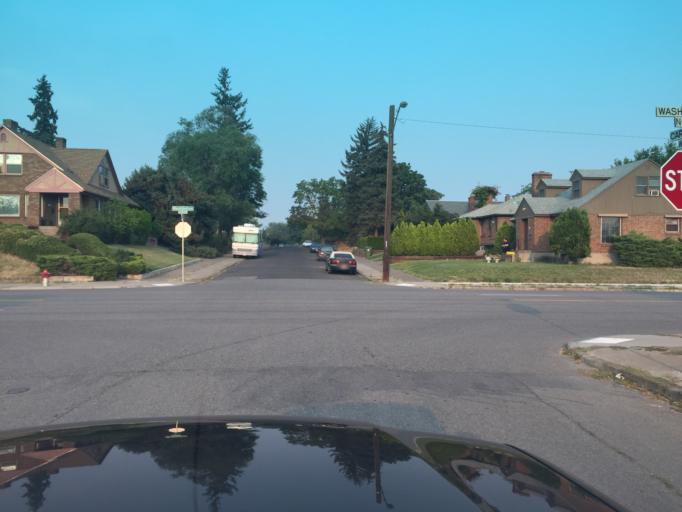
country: US
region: Washington
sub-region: Spokane County
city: Spokane
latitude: 47.6793
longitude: -117.4176
